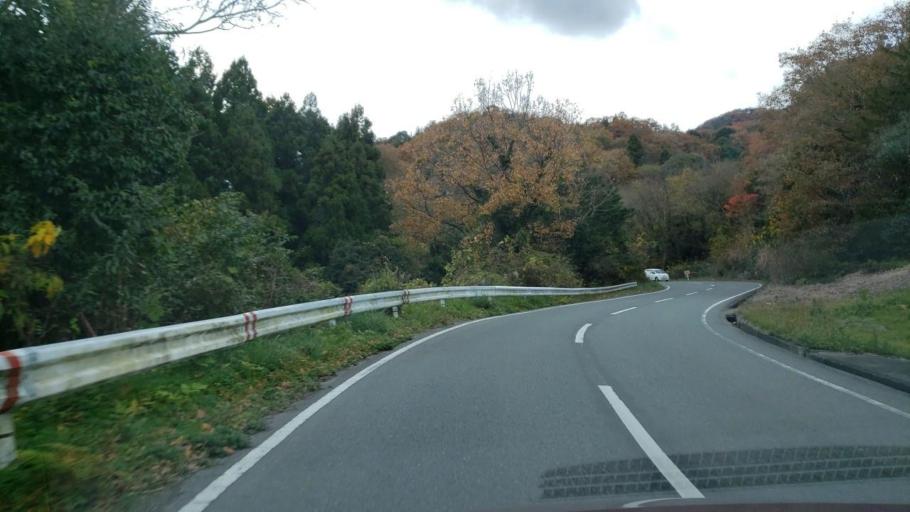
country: JP
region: Tokushima
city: Wakimachi
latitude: 34.0905
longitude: 134.2039
